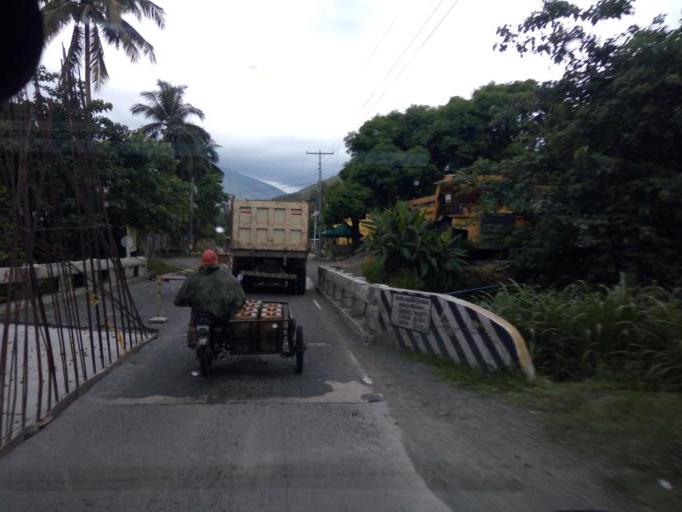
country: PH
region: Cagayan Valley
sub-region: Province of Nueva Vizcaya
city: Santa Fe
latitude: 16.0735
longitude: 120.9427
